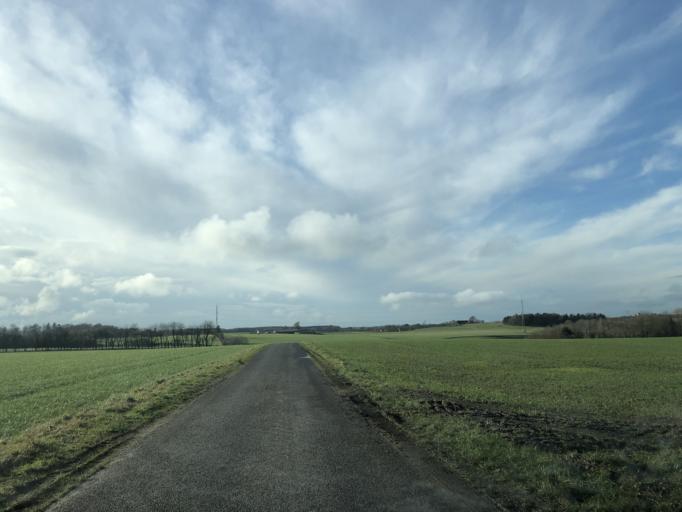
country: DK
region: North Denmark
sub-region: Vesthimmerland Kommune
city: Alestrup
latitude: 56.6443
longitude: 9.6299
